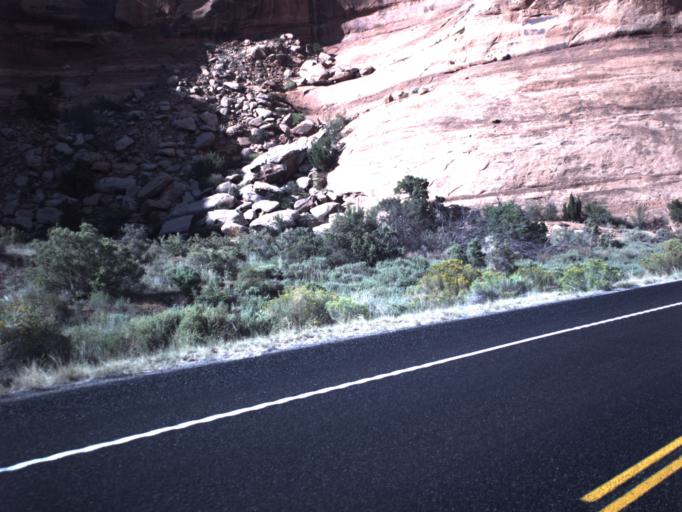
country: US
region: Utah
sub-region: Grand County
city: Moab
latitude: 38.6521
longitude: -109.7204
